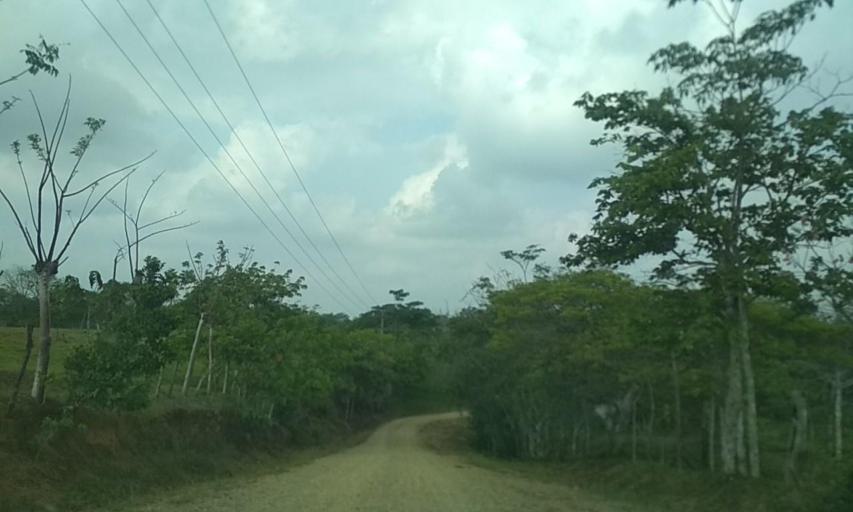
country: MX
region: Tabasco
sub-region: Huimanguillo
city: Francisco Rueda
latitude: 17.6555
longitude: -93.7589
